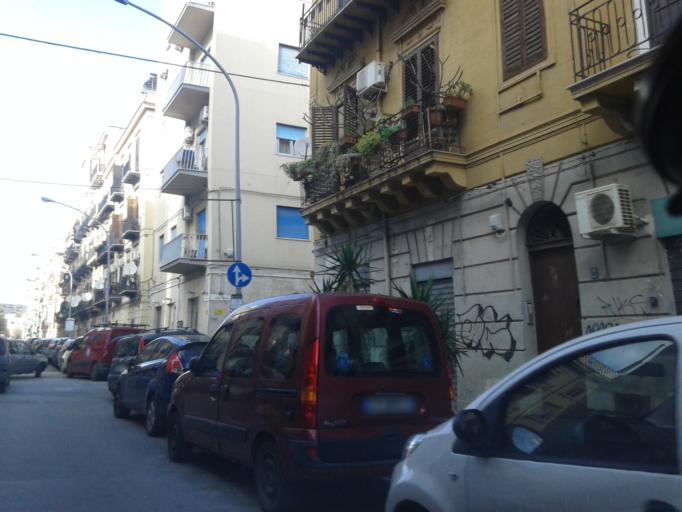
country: IT
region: Sicily
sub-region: Palermo
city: Palermo
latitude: 38.1202
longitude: 13.3454
